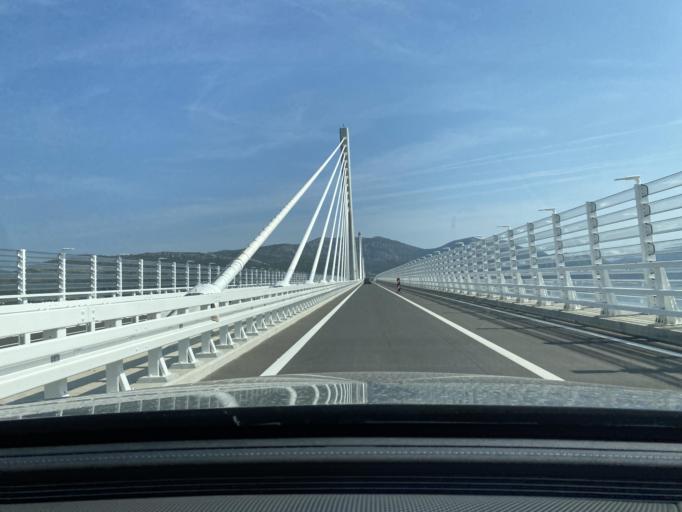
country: BA
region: Federation of Bosnia and Herzegovina
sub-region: Hercegovacko-Bosanski Kanton
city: Neum
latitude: 42.9275
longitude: 17.5319
